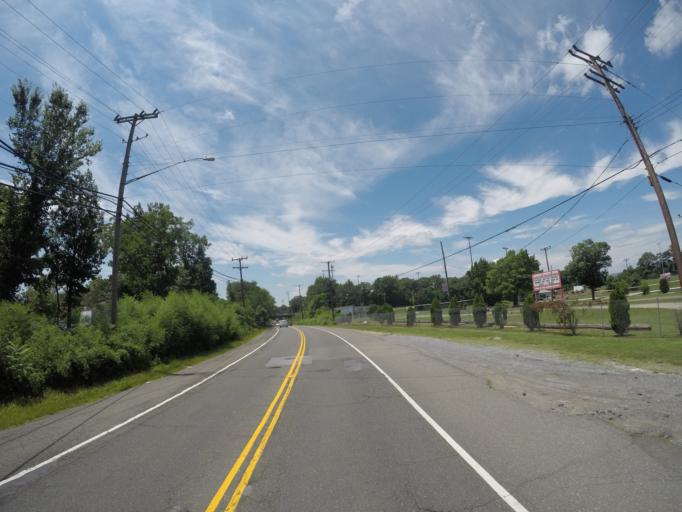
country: US
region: Maryland
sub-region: Prince George's County
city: New Carrollton
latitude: 38.9794
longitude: -76.8715
